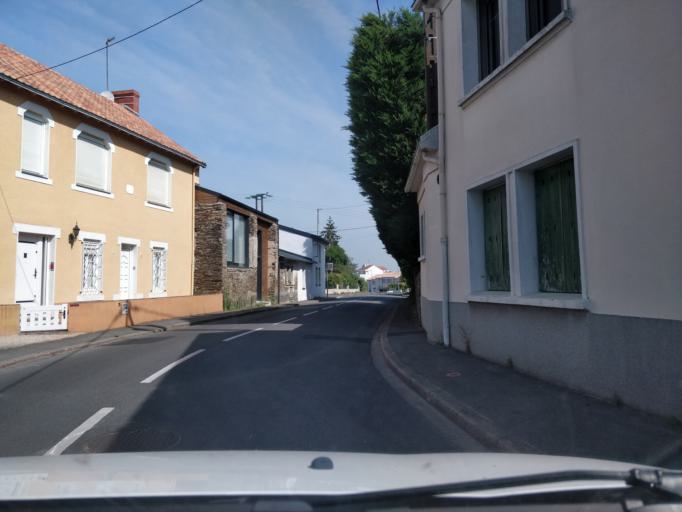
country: FR
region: Pays de la Loire
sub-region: Departement de la Loire-Atlantique
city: Saint-Sebastien-sur-Loire
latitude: 47.2028
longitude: -1.4951
